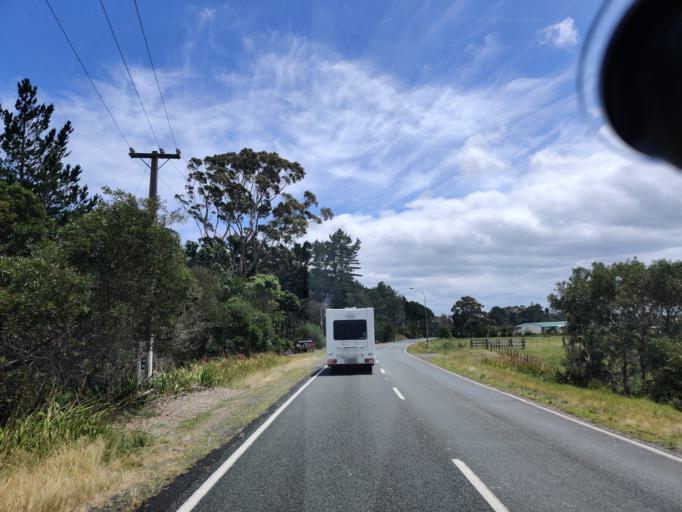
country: NZ
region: Northland
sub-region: Far North District
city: Kaitaia
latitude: -34.7451
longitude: 173.0478
